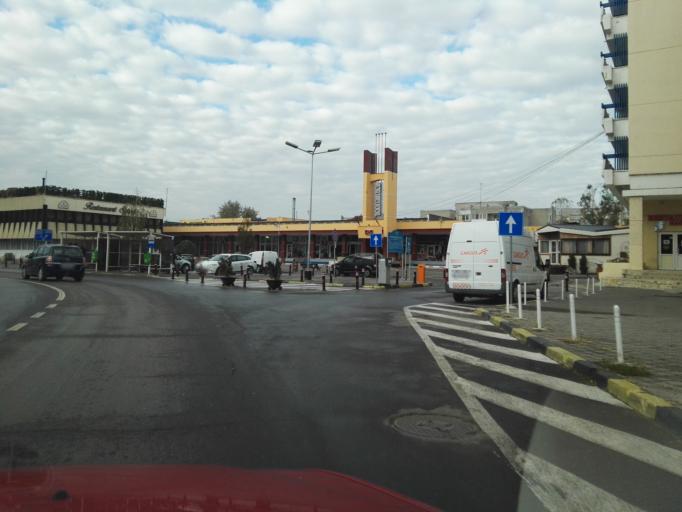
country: RO
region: Ilfov
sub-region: Comuna Magurele
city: Magurele
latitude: 44.3506
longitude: 26.0312
